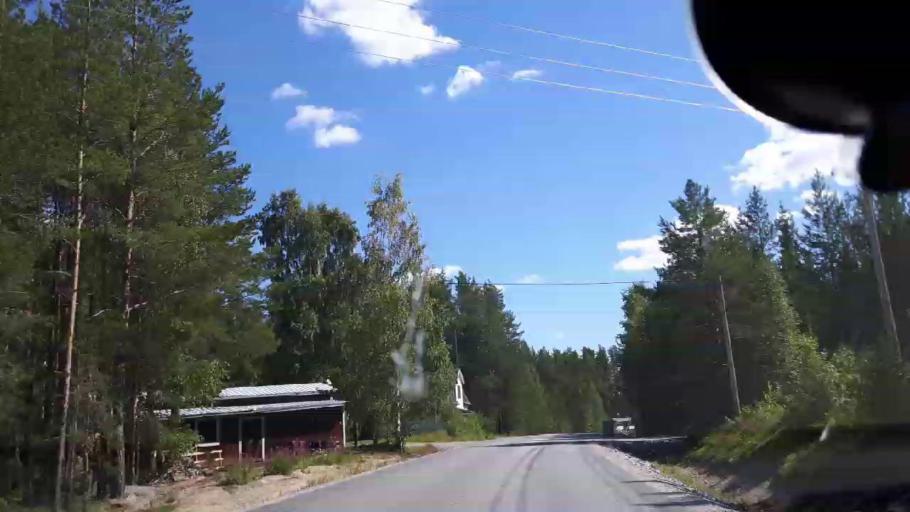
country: SE
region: Vaesternorrland
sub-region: Ange Kommun
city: Fransta
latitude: 62.7000
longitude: 16.3892
